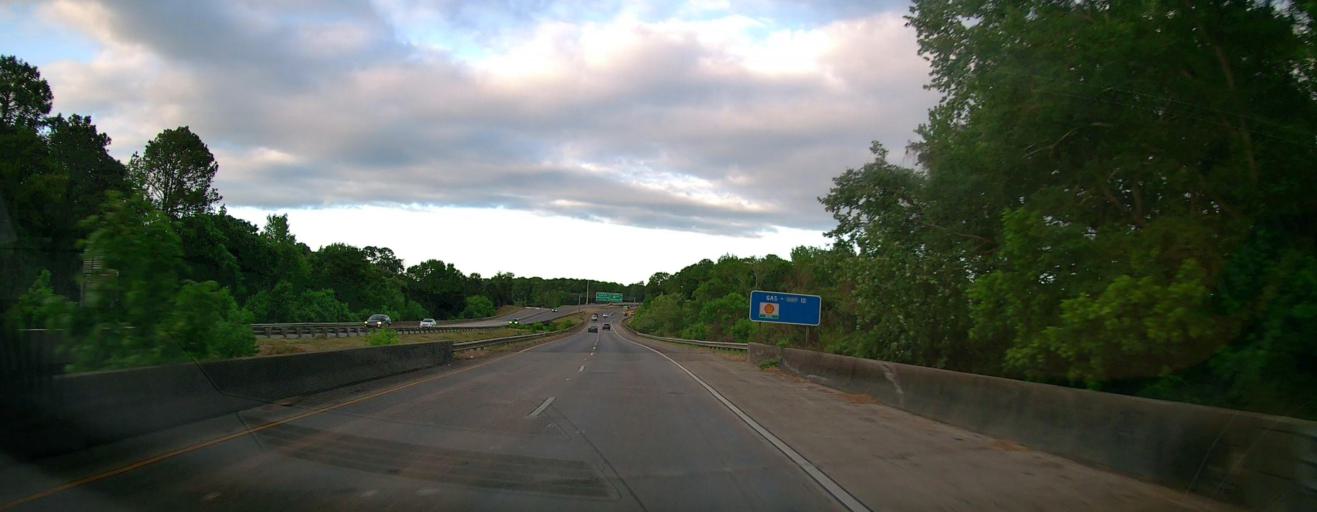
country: US
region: Georgia
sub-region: Clarke County
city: Athens
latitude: 33.9757
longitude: -83.3841
